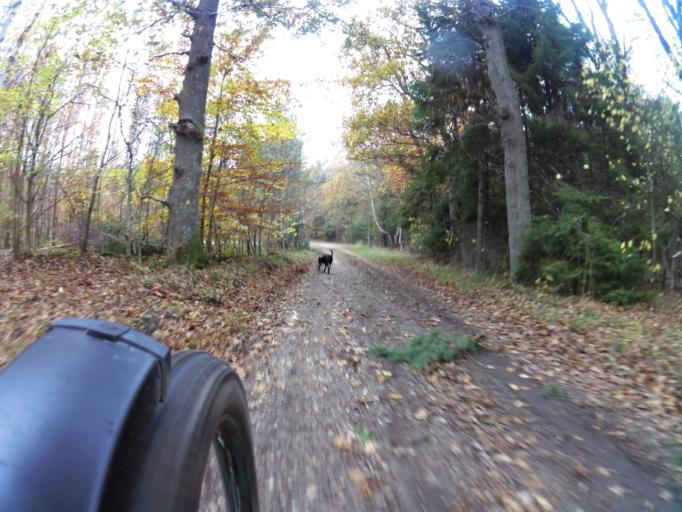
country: PL
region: Pomeranian Voivodeship
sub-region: Powiat pucki
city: Krokowa
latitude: 54.8309
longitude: 18.1036
